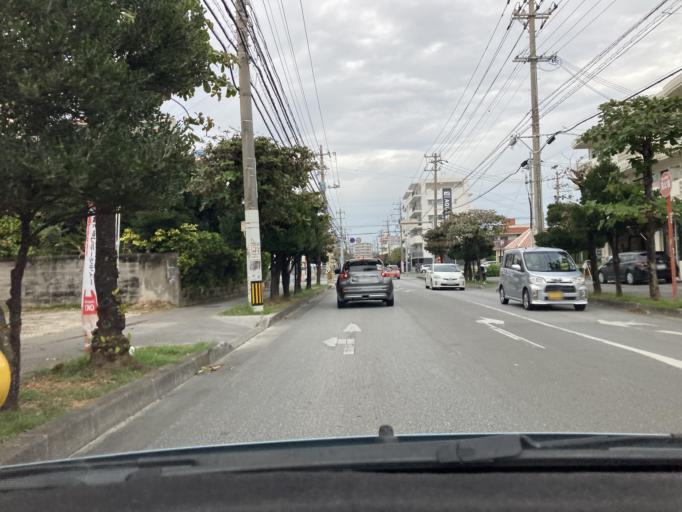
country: JP
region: Okinawa
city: Chatan
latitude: 26.3060
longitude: 127.7606
